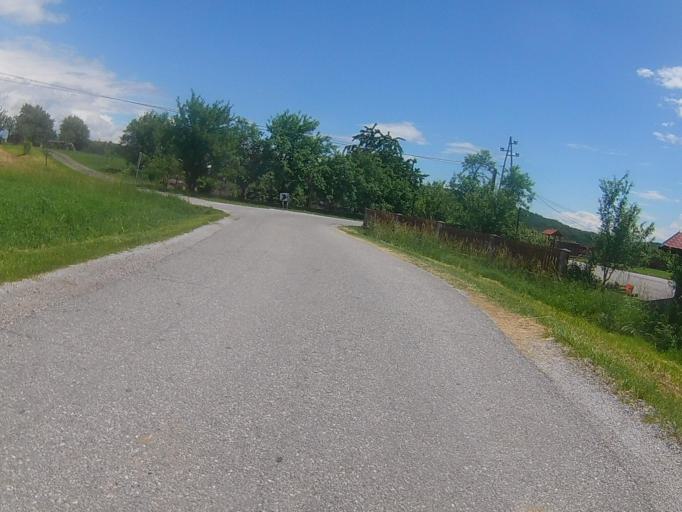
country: SI
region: Duplek
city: Zgornji Duplek
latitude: 46.5543
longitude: 15.7223
